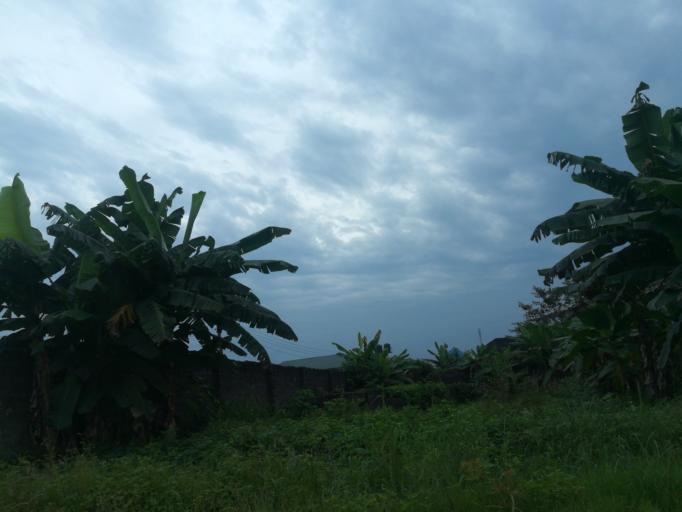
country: NG
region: Rivers
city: Port Harcourt
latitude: 4.7982
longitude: 6.9541
